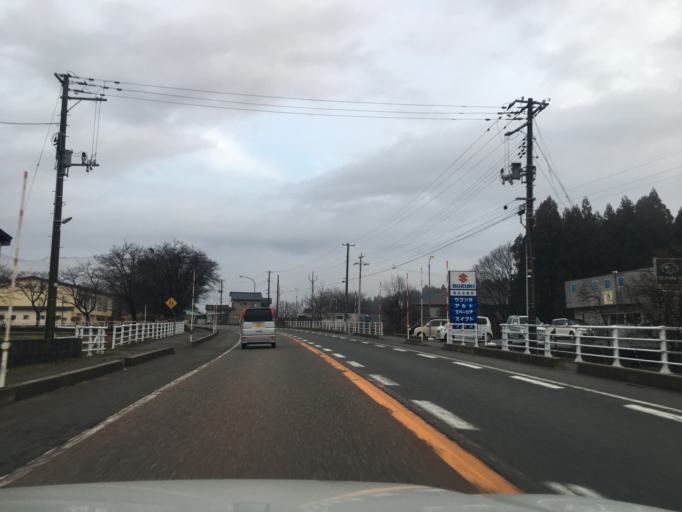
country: JP
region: Niigata
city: Murakami
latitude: 38.3315
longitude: 139.5553
